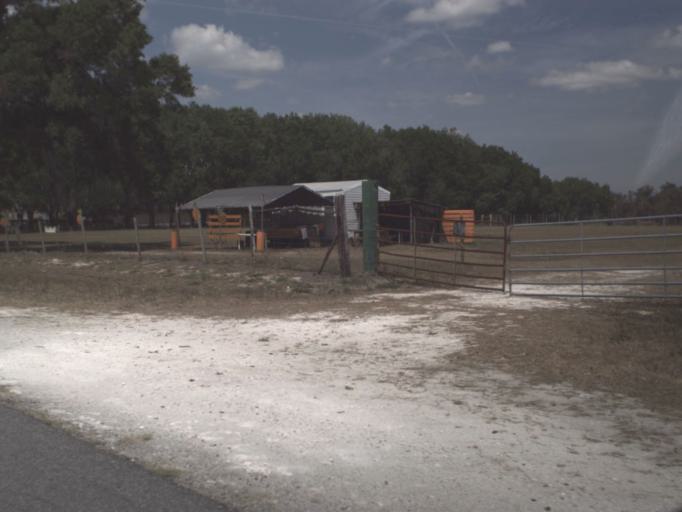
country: US
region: Florida
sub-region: Lake County
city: Mascotte
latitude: 28.5800
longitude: -81.9502
